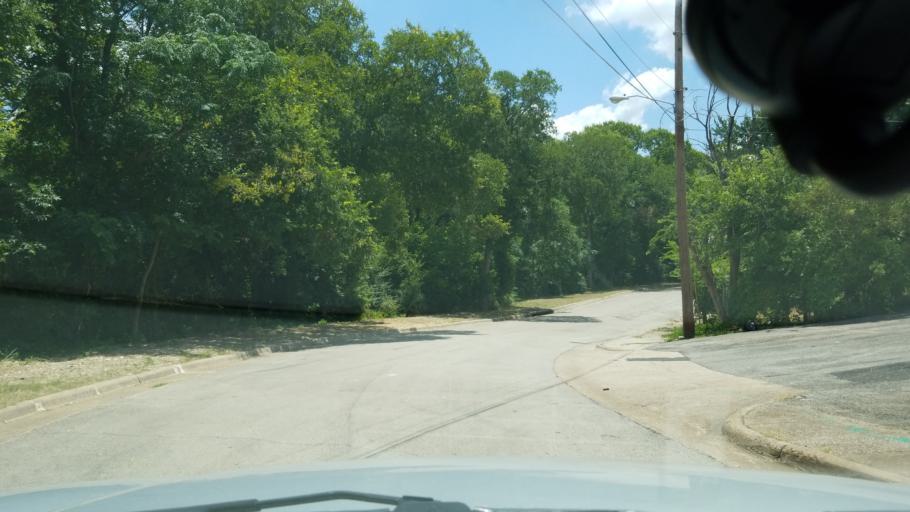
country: US
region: Texas
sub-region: Dallas County
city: Cockrell Hill
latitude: 32.6924
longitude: -96.8798
